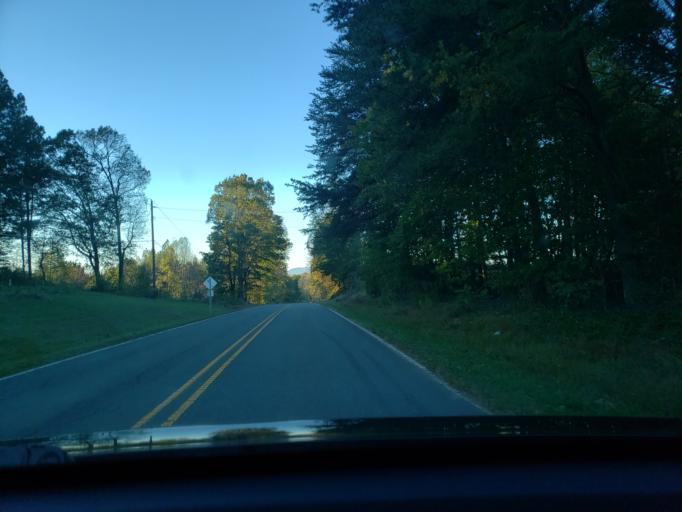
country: US
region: North Carolina
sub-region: Forsyth County
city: Walkertown
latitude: 36.2294
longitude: -80.1990
